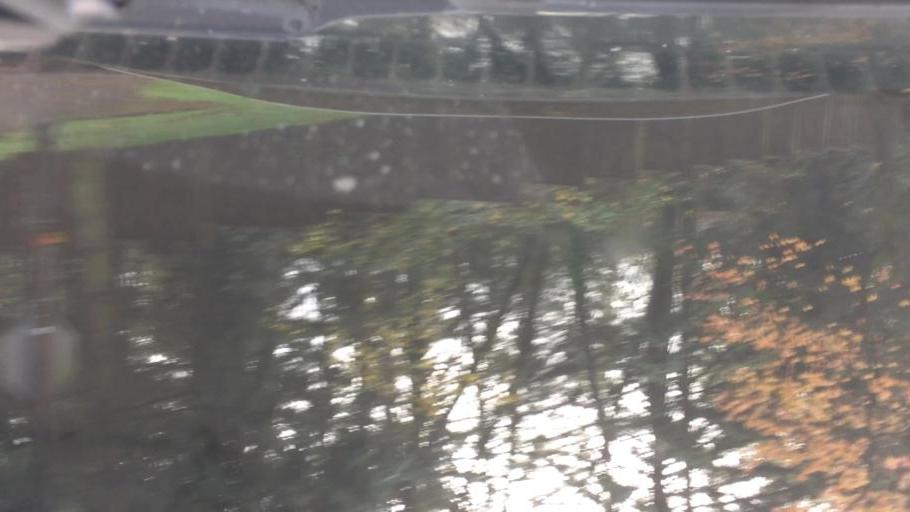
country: US
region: Oregon
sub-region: Lane County
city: Eugene
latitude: 44.0271
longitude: -123.1177
